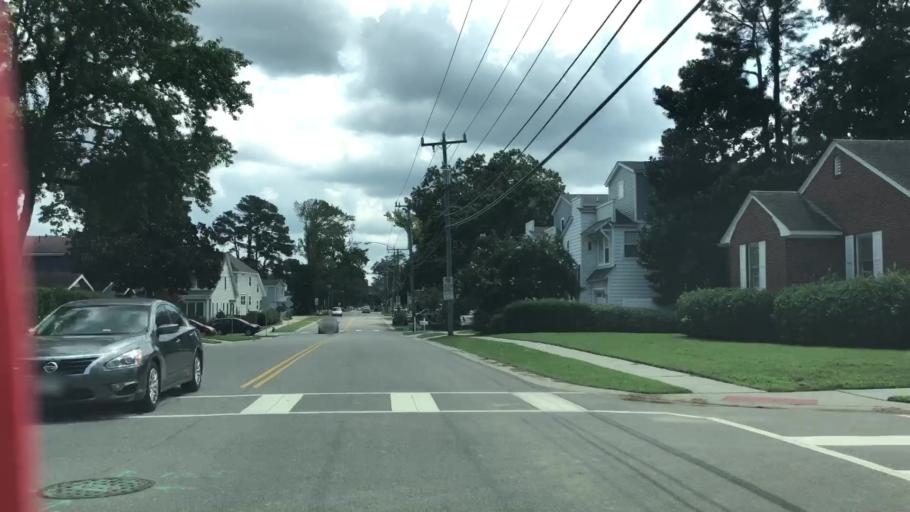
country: US
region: Virginia
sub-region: City of Virginia Beach
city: Virginia Beach
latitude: 36.8396
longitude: -75.9799
